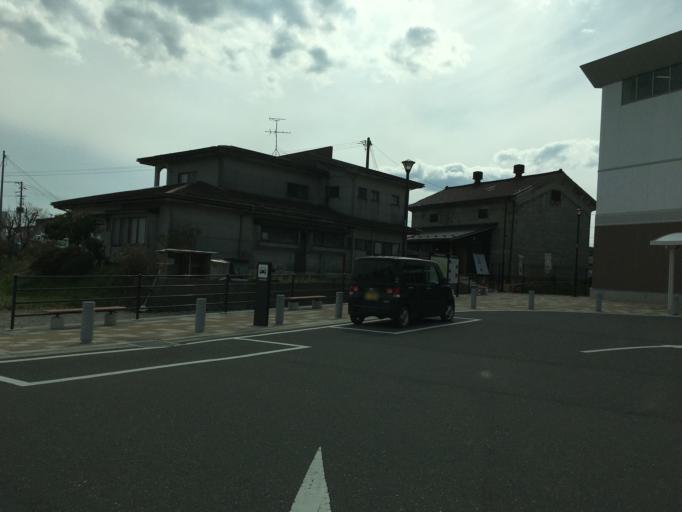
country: JP
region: Fukushima
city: Nihommatsu
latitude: 37.6121
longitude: 140.4671
